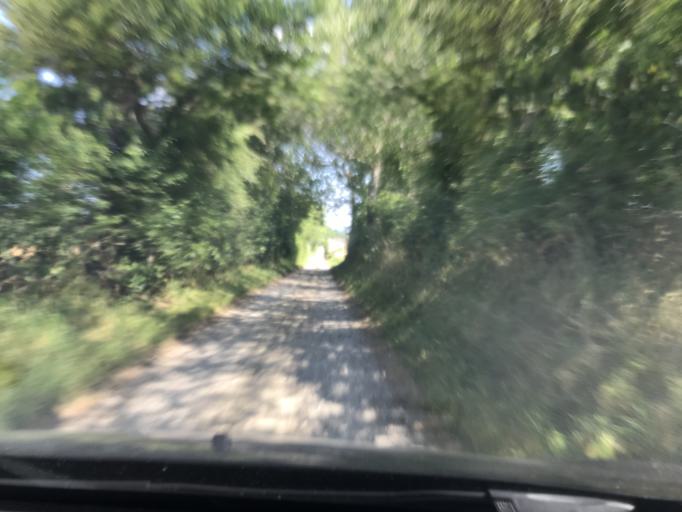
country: DK
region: South Denmark
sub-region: AEro Kommune
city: AEroskobing
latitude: 54.8820
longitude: 10.3623
